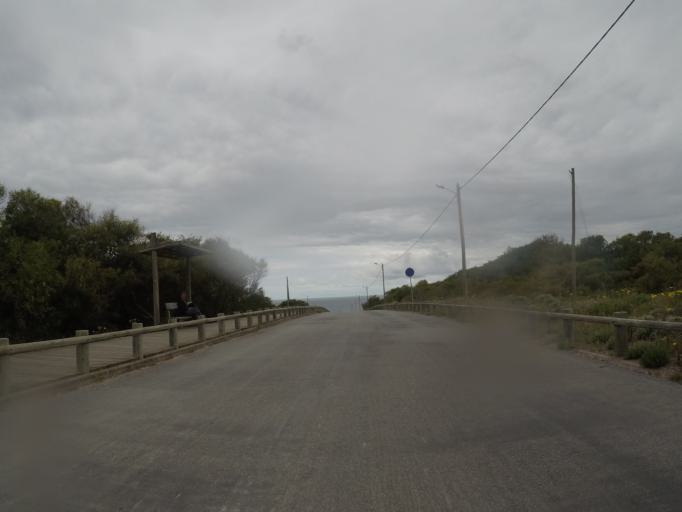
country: PT
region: Beja
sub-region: Odemira
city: Vila Nova de Milfontes
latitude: 37.6527
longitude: -8.7974
